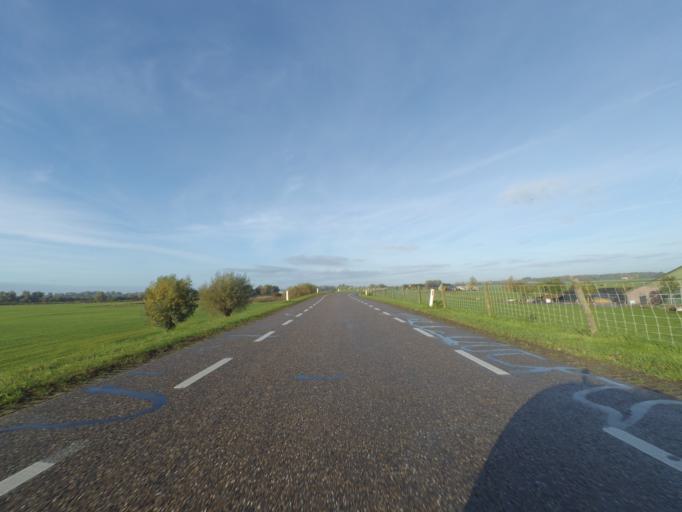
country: NL
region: Utrecht
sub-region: Gemeente Utrechtse Heuvelrug
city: Leersum
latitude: 51.9761
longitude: 5.3923
